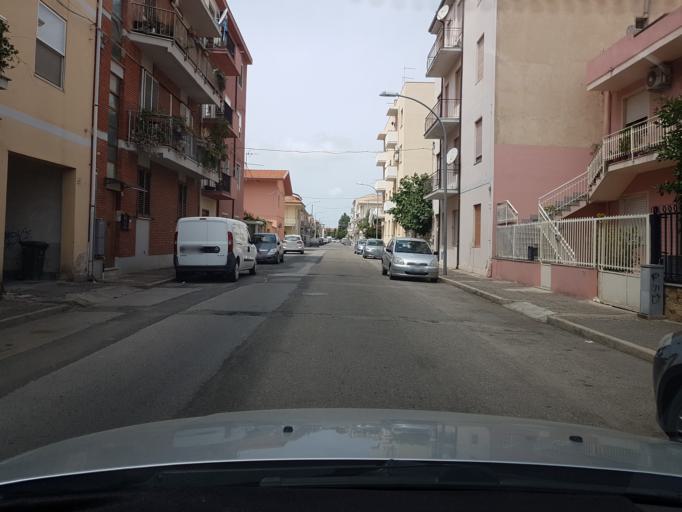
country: IT
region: Sardinia
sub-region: Provincia di Oristano
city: Oristano
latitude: 39.9102
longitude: 8.5952
